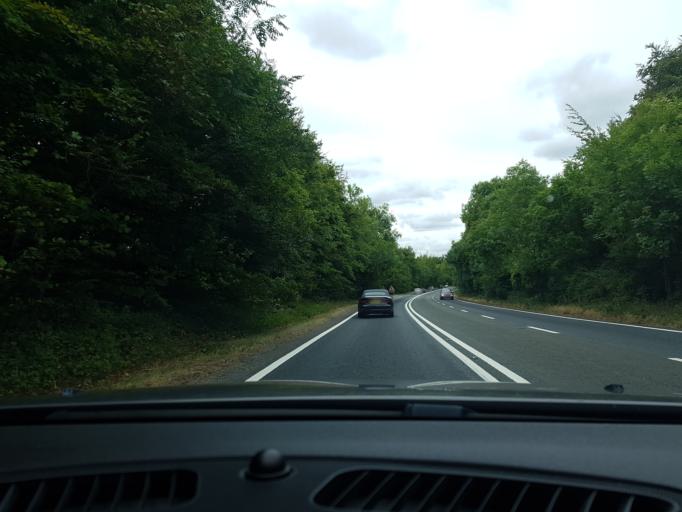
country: GB
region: England
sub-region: Hampshire
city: Kingsclere
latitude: 51.3148
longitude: -1.2051
